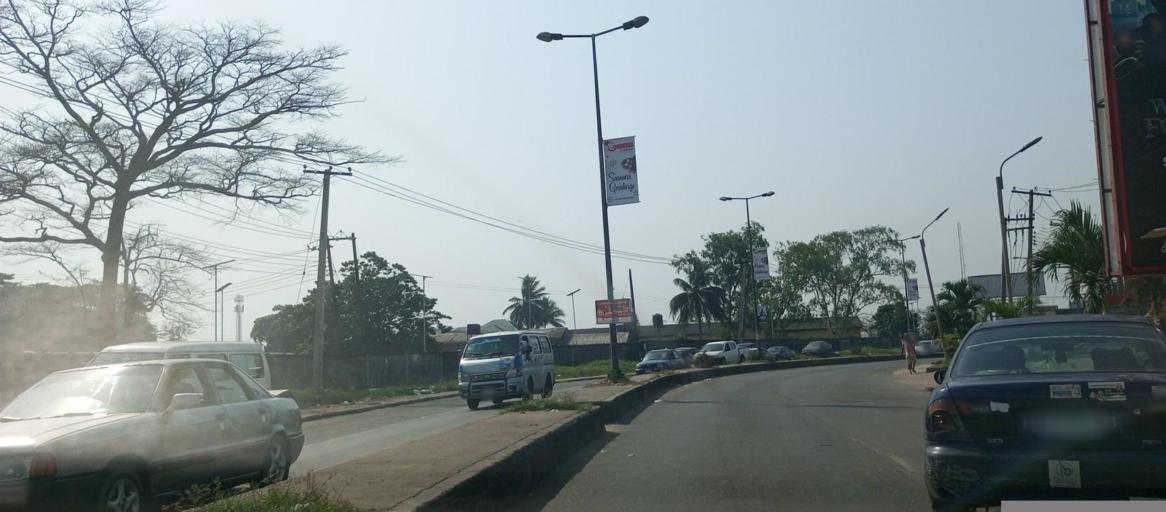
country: NG
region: Rivers
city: Emuoha
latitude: 4.8957
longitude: 6.9071
